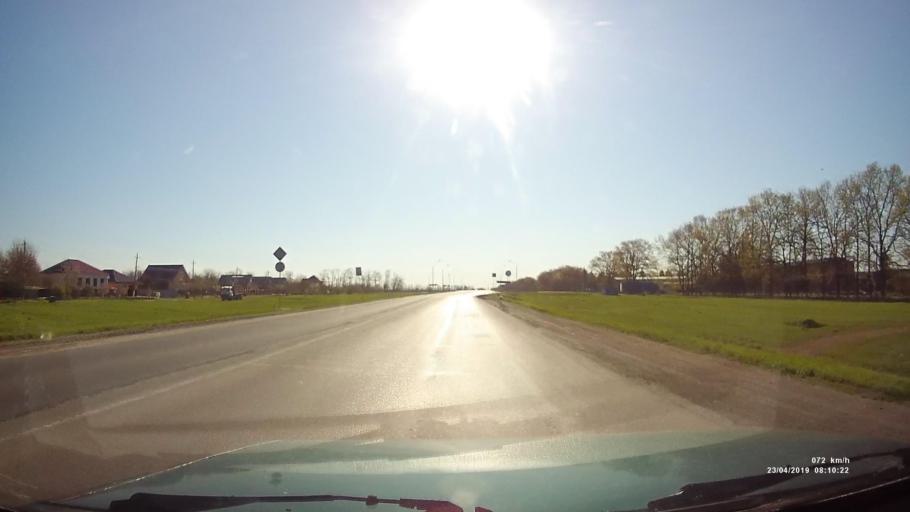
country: RU
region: Rostov
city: Yegorlykskaya
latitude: 46.5561
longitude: 40.6804
